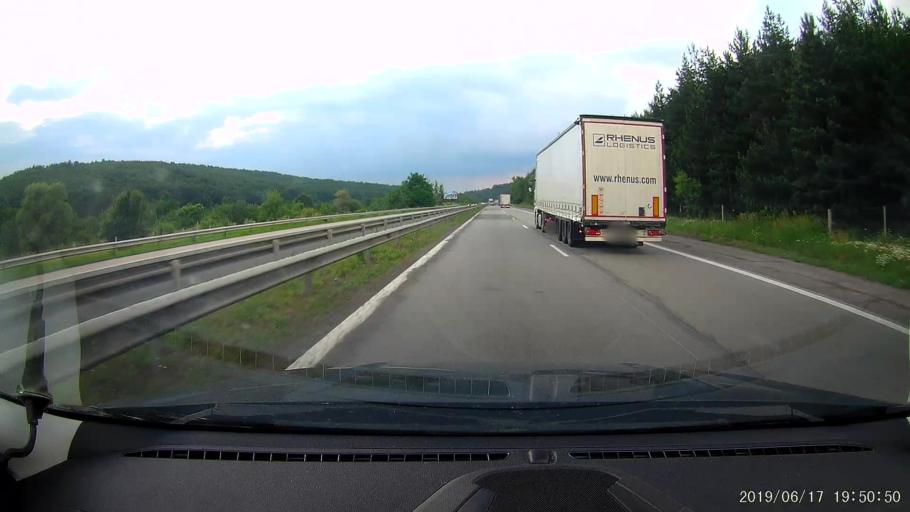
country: BG
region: Sofiya
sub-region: Obshtina Ikhtiman
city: Ikhtiman
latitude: 42.4997
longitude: 23.7718
